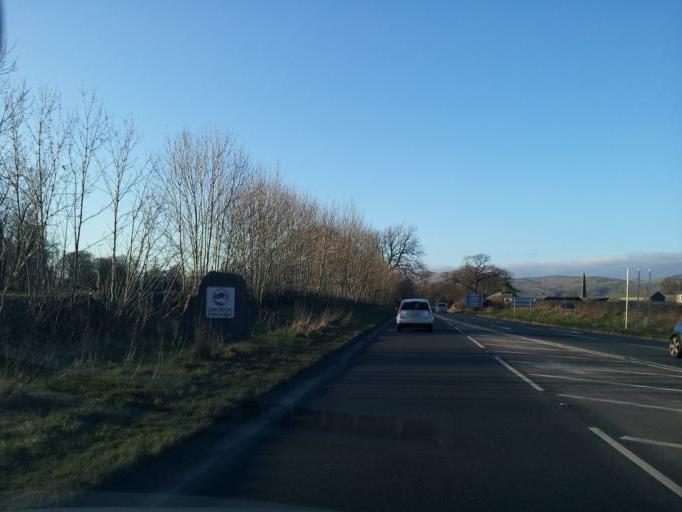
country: GB
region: England
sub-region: Cumbria
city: Kendal
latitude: 54.3459
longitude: -2.7756
